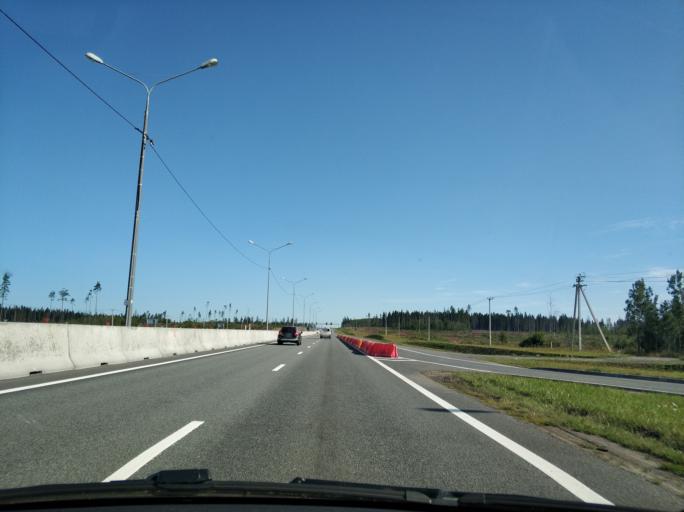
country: RU
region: Leningrad
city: Sosnovo
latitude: 60.4762
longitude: 30.1960
